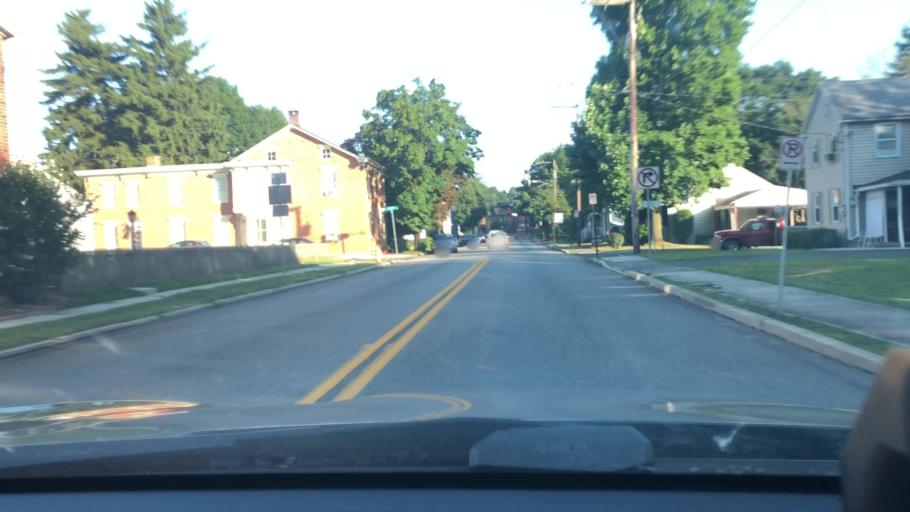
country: US
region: Pennsylvania
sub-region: Cumberland County
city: Mechanicsburg
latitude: 40.2143
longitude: -77.0025
